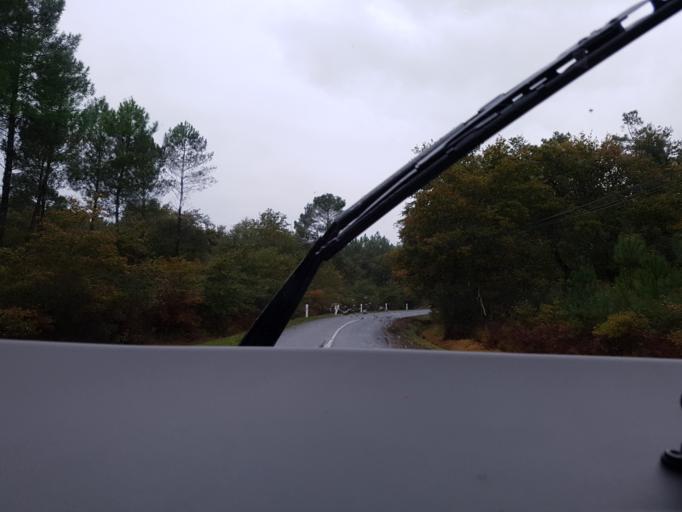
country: FR
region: Aquitaine
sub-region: Departement de la Gironde
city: Saint-Symphorien
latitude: 44.3449
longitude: -0.6115
